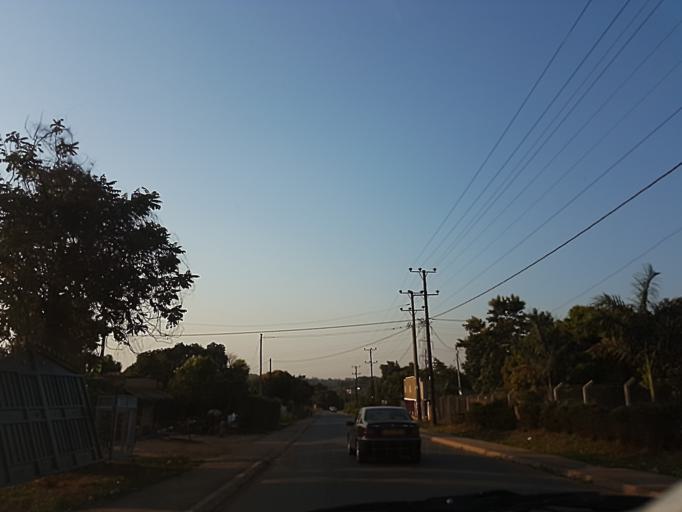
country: UG
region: Central Region
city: Kampala Central Division
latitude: 0.4003
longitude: 32.5909
